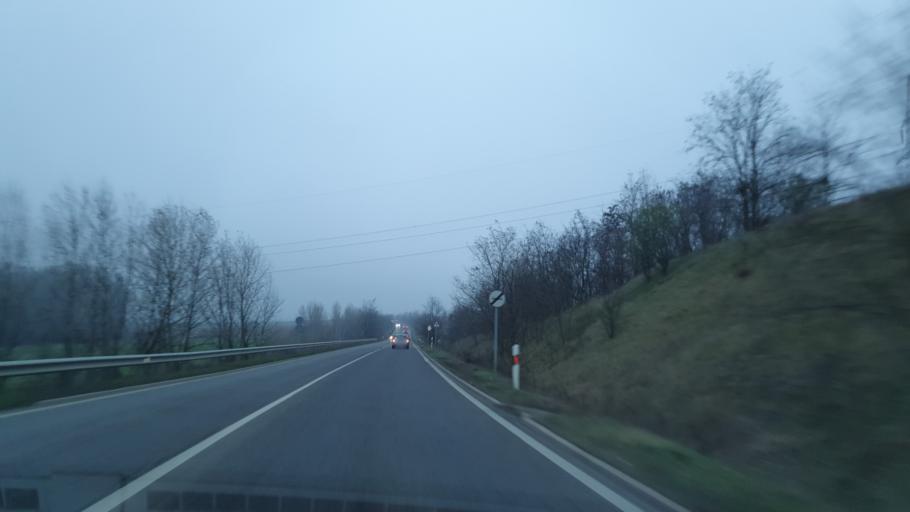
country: HU
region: Budapest
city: Budapest XVI. keruelet
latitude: 47.5530
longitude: 19.1886
